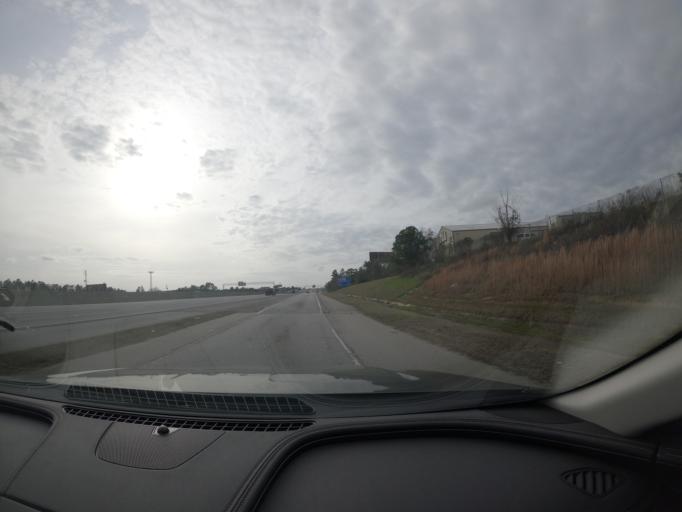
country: US
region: Georgia
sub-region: Columbia County
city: Martinez
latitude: 33.4872
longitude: -82.1123
